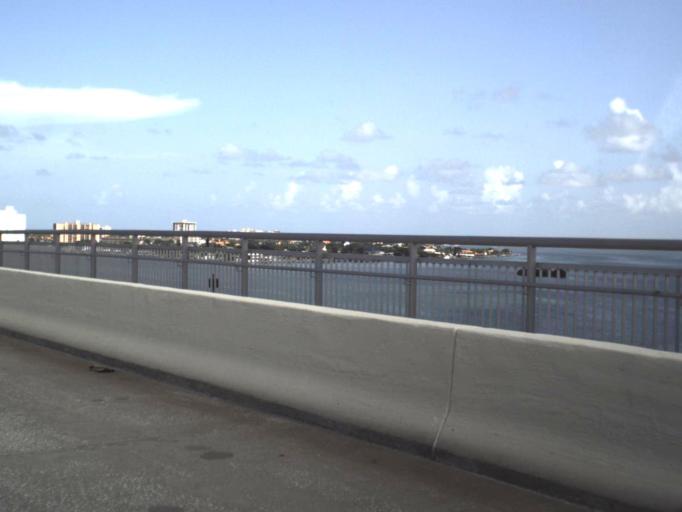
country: US
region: Florida
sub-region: Pinellas County
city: Clearwater
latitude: 27.9663
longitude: -82.8056
